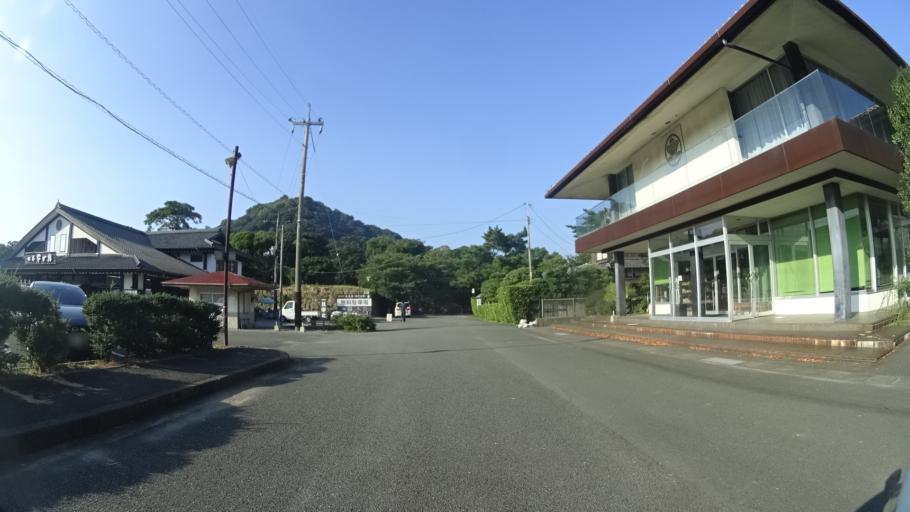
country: JP
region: Yamaguchi
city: Hagi
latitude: 34.4154
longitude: 131.3826
